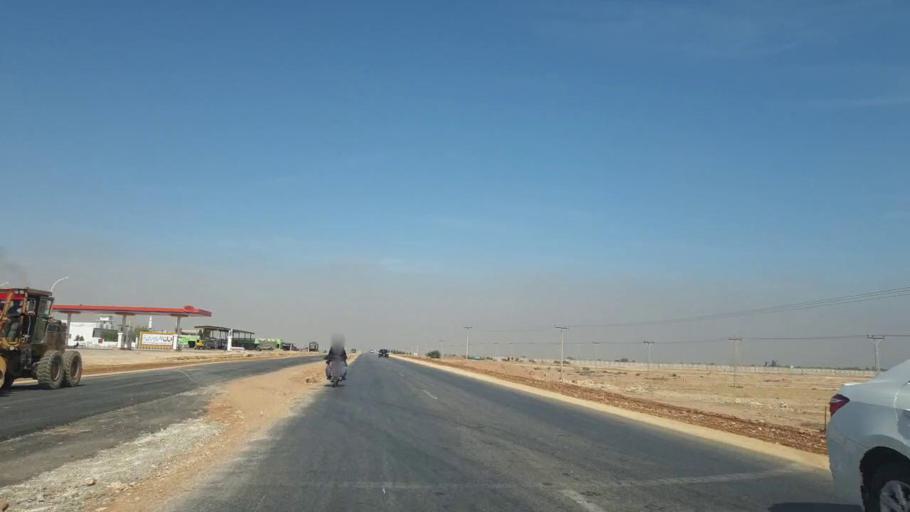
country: PK
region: Sindh
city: Jamshoro
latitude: 25.4987
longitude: 68.2726
